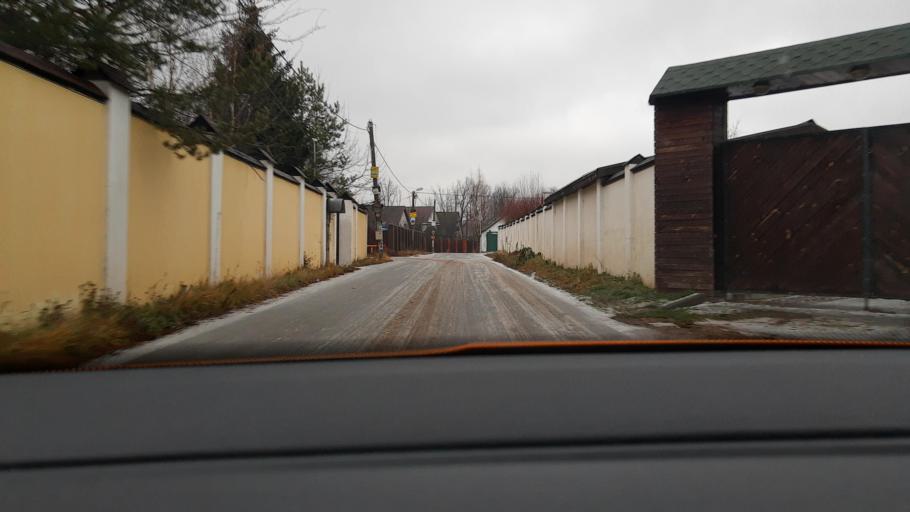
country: RU
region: Moscow
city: Severnyy
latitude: 55.9573
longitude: 37.5593
